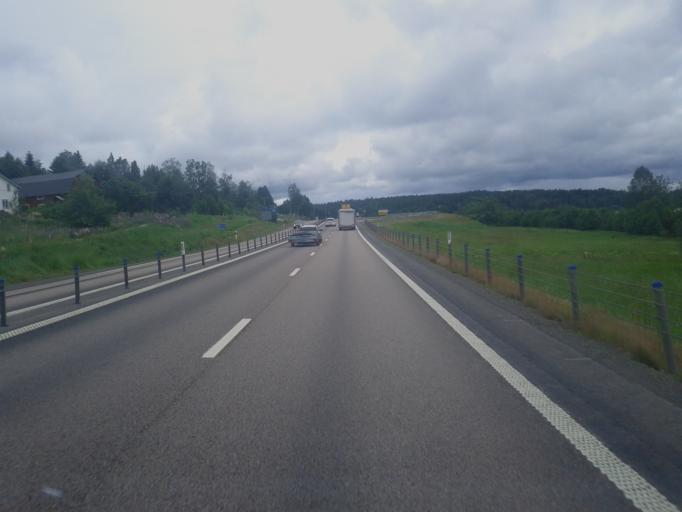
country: SE
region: Vaesternorrland
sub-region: Timra Kommun
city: Soraker
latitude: 62.5581
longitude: 17.6578
